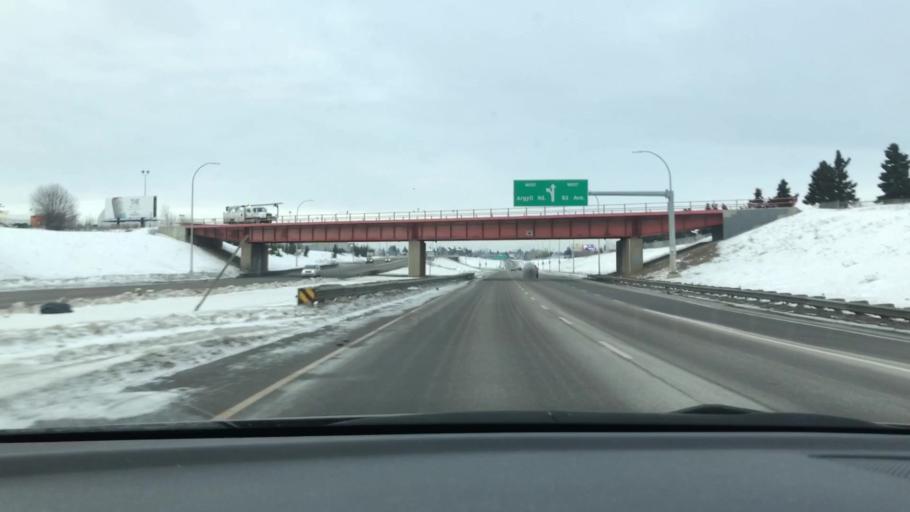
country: CA
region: Alberta
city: Edmonton
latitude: 53.5144
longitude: -113.4231
